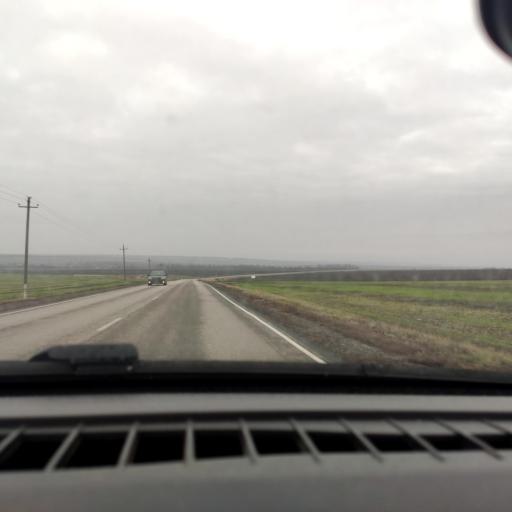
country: RU
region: Belgorod
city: Ilovka
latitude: 50.7771
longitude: 38.7913
